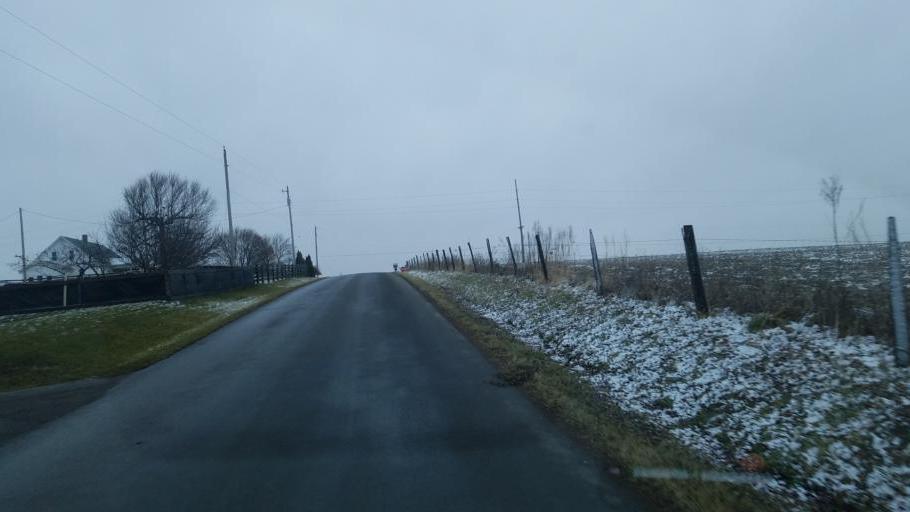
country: US
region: Ohio
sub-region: Wayne County
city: Apple Creek
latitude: 40.7102
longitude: -81.8621
